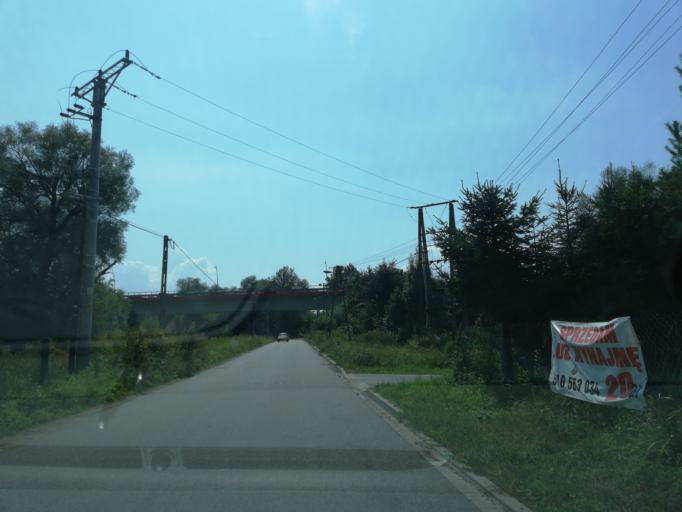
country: PL
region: Lesser Poland Voivodeship
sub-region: Powiat nowosadecki
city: Chelmiec
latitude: 49.6426
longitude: 20.6759
